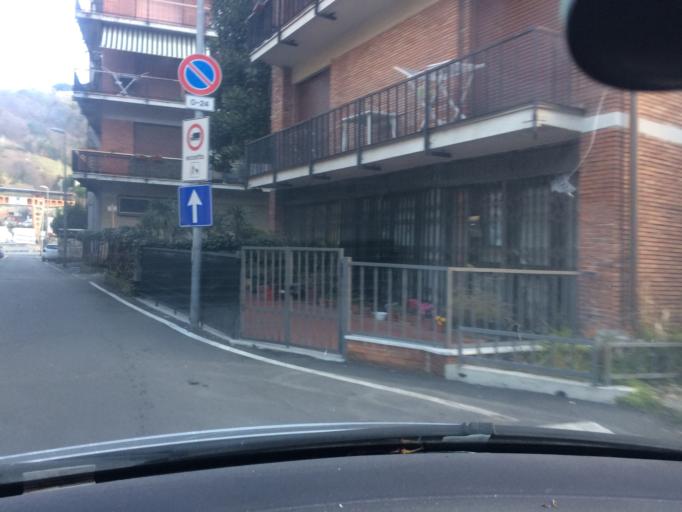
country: IT
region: Tuscany
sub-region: Provincia di Massa-Carrara
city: Carrara
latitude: 44.0708
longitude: 10.0886
